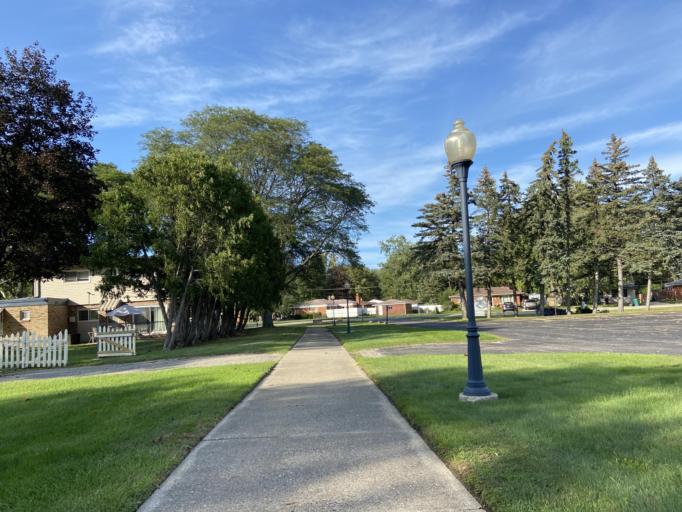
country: US
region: Michigan
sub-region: Oakland County
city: Farmington
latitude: 42.4504
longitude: -83.3229
